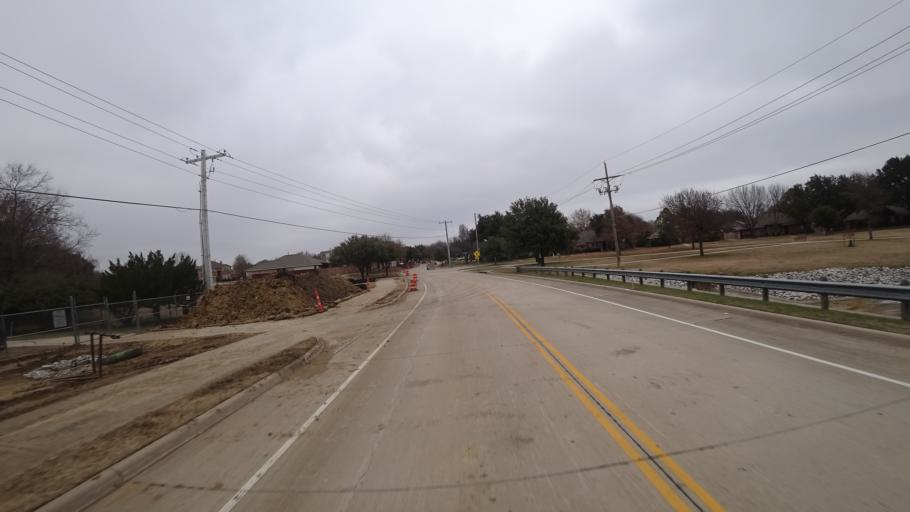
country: US
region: Texas
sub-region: Denton County
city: Highland Village
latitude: 33.0570
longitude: -97.0445
